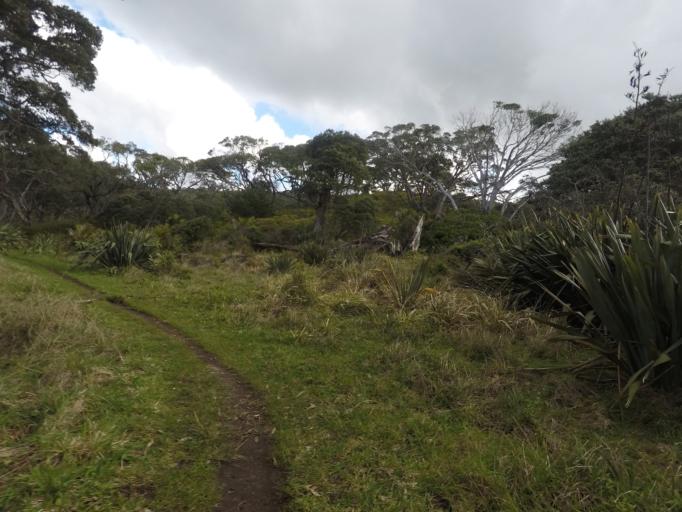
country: NZ
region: Bay of Plenty
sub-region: Western Bay of Plenty District
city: Waihi Beach
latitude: -37.3842
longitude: 175.9382
